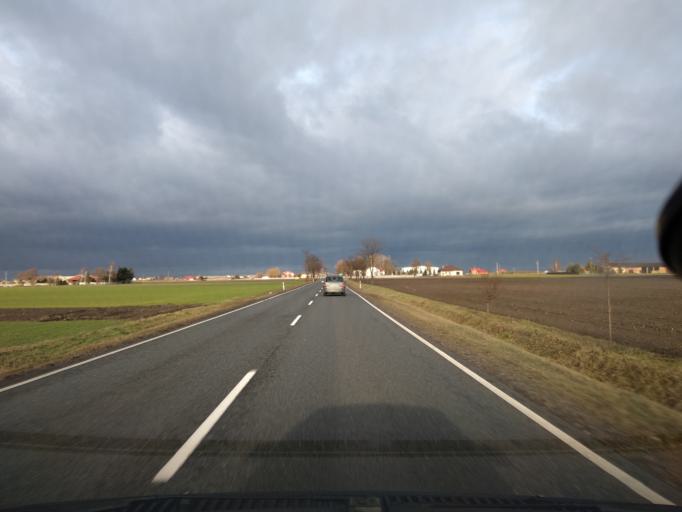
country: PL
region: Greater Poland Voivodeship
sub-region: Powiat kaliski
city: Stawiszyn
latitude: 51.8850
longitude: 18.1006
